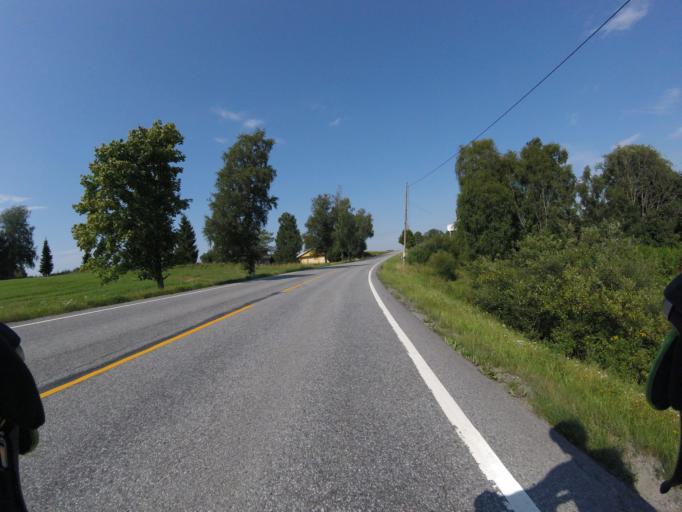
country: NO
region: Akershus
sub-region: Ullensaker
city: Klofta
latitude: 60.0537
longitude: 11.1176
